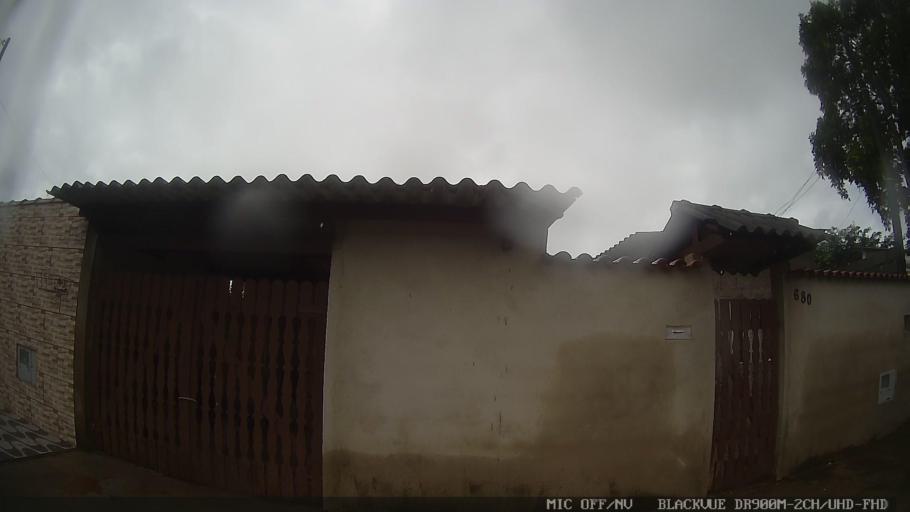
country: BR
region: Sao Paulo
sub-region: Itanhaem
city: Itanhaem
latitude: -24.1831
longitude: -46.8128
